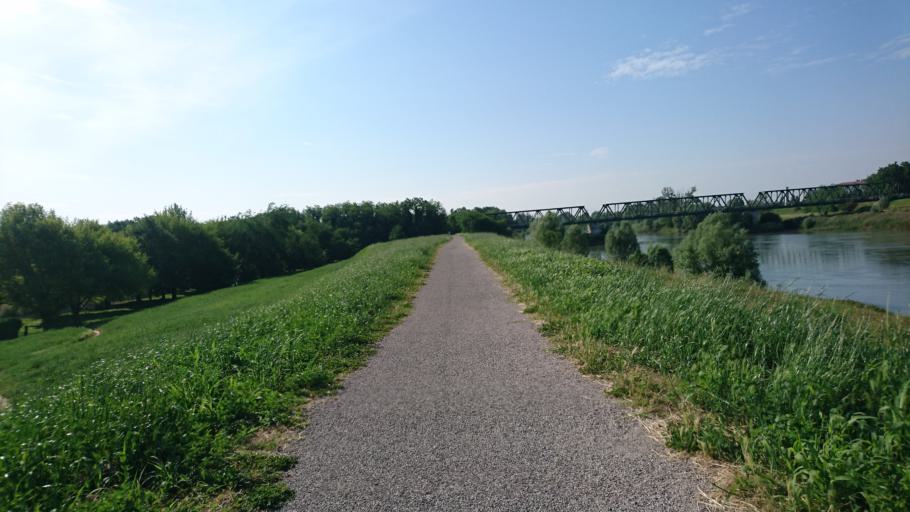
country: IT
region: Veneto
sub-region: Provincia di Verona
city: Boschi Sant'Anna
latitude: 45.1932
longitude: 11.3155
